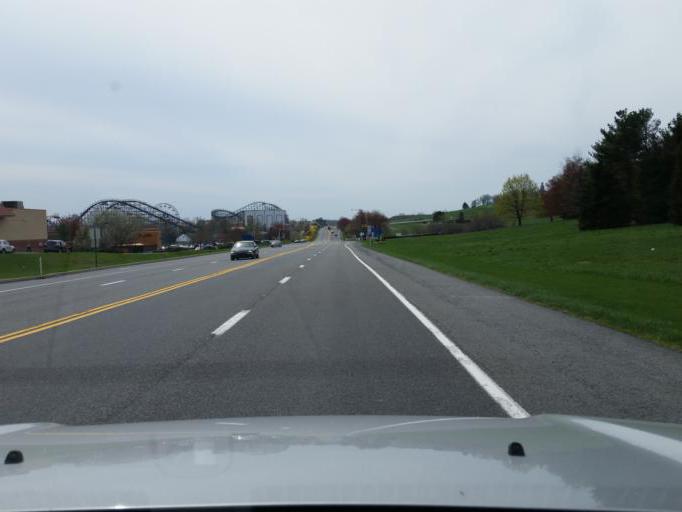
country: US
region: Pennsylvania
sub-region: Dauphin County
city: Hershey
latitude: 40.2959
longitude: -76.6489
